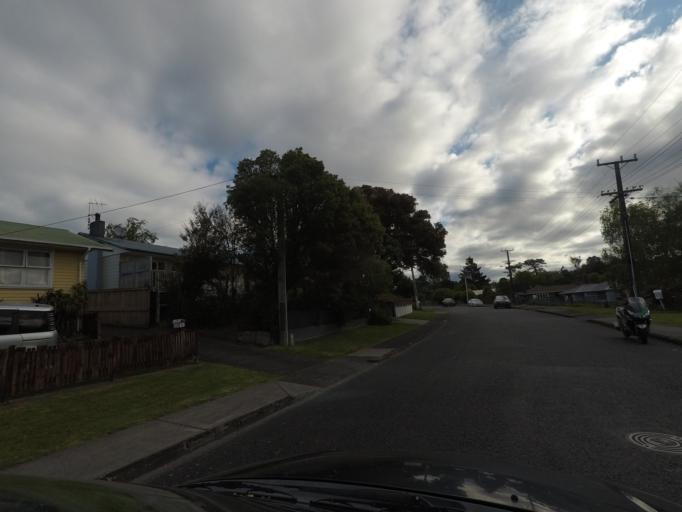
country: NZ
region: Auckland
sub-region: Auckland
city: Rosebank
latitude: -36.8826
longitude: 174.6561
